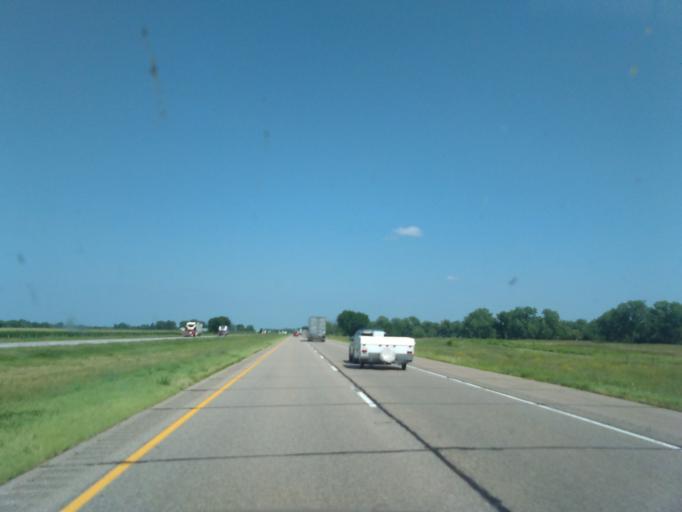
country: US
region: Nebraska
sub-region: Buffalo County
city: Kearney
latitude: 40.6744
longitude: -99.2416
